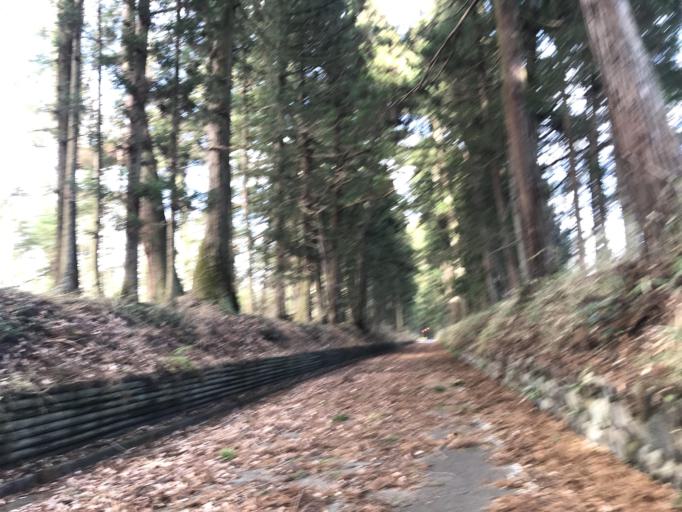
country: JP
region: Tochigi
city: Imaichi
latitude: 36.6823
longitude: 139.7191
